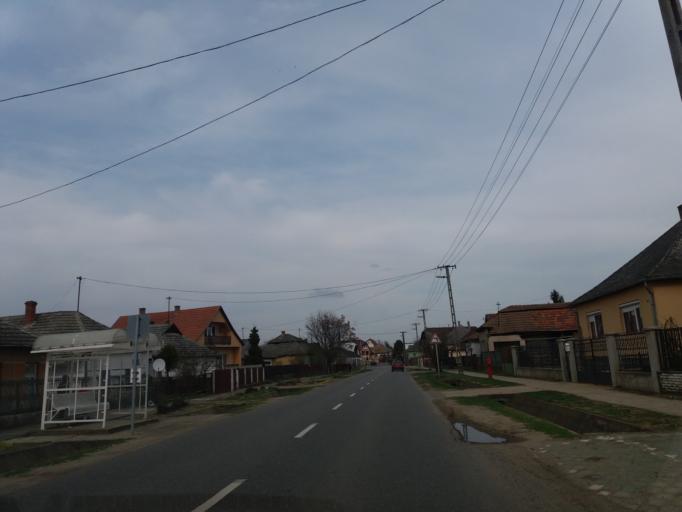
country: HU
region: Szabolcs-Szatmar-Bereg
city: Anarcs
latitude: 48.1748
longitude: 22.0987
